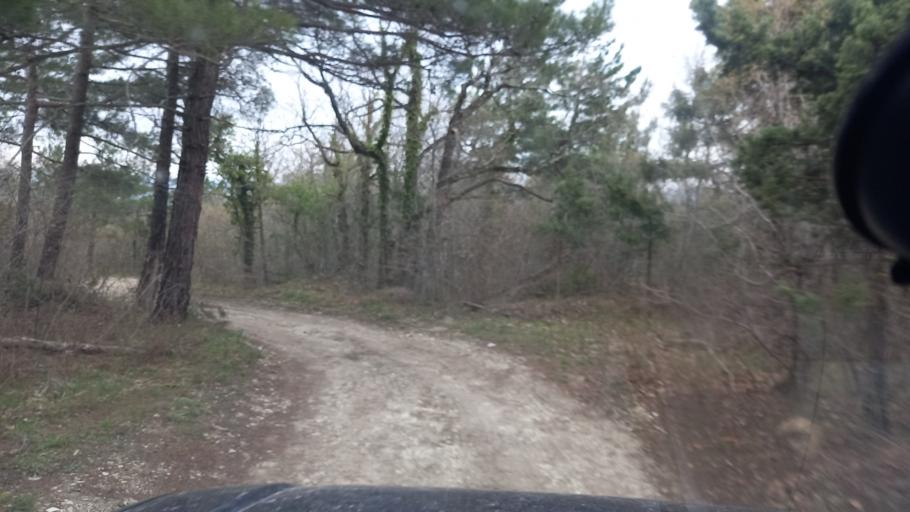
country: RU
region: Krasnodarskiy
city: Dzhubga
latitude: 44.3192
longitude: 38.6788
